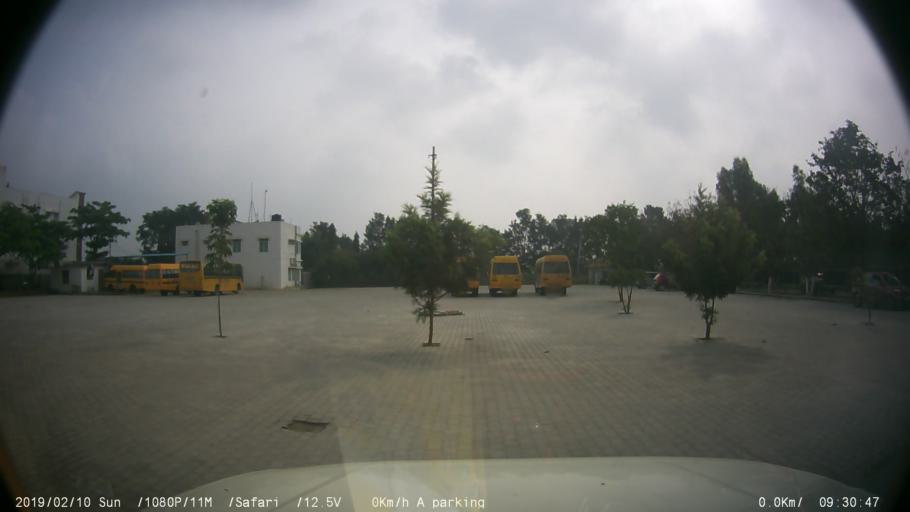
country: IN
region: Karnataka
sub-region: Bangalore Urban
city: Anekal
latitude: 12.8254
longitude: 77.6222
